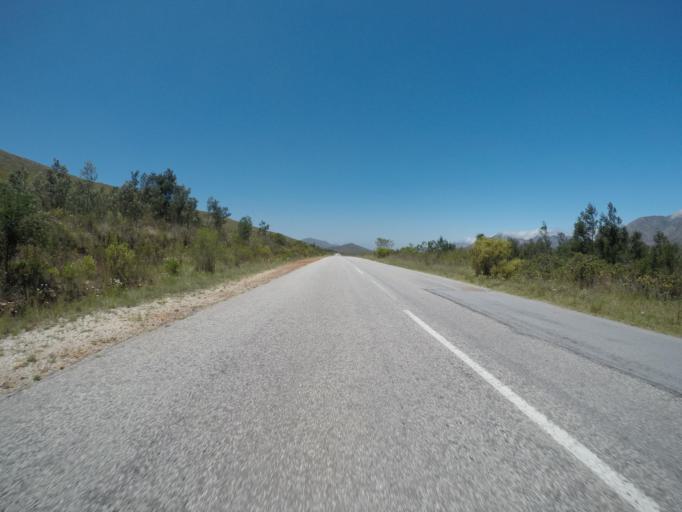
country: ZA
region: Eastern Cape
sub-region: Cacadu District Municipality
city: Kareedouw
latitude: -33.8486
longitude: 23.9639
